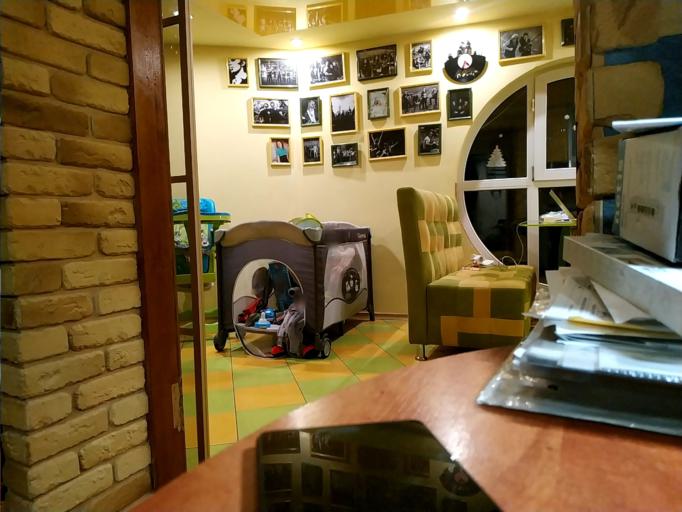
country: RU
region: Orjol
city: Naryshkino
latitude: 53.0239
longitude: 35.6882
